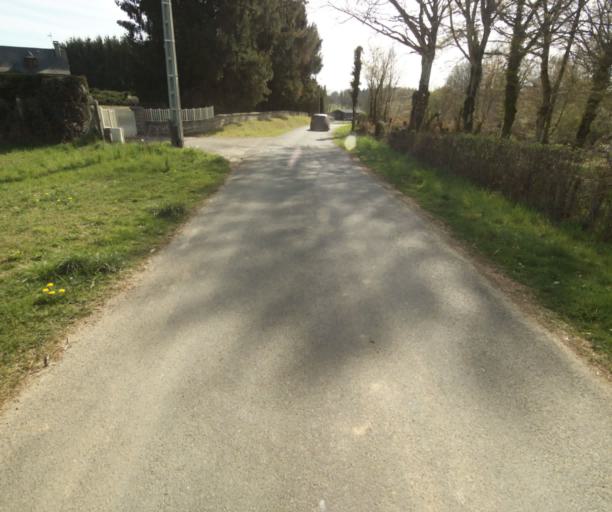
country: FR
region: Limousin
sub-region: Departement de la Correze
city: Naves
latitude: 45.3393
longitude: 1.7408
